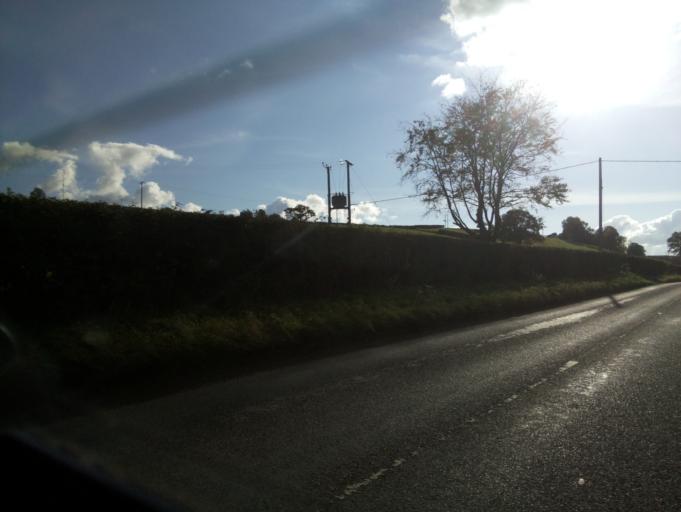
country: GB
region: Wales
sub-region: Sir Powys
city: Hay
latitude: 52.0504
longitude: -3.1799
